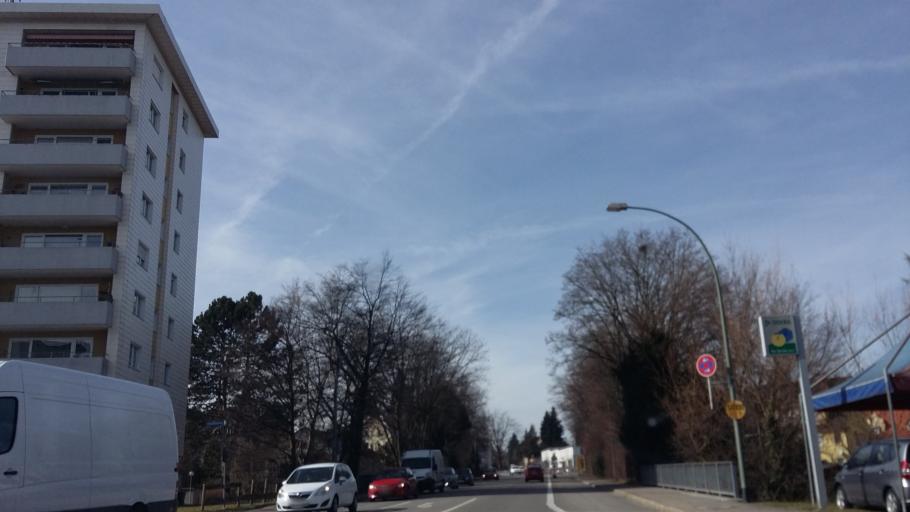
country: DE
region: Bavaria
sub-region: Swabia
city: Lindau
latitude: 47.5530
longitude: 9.6963
